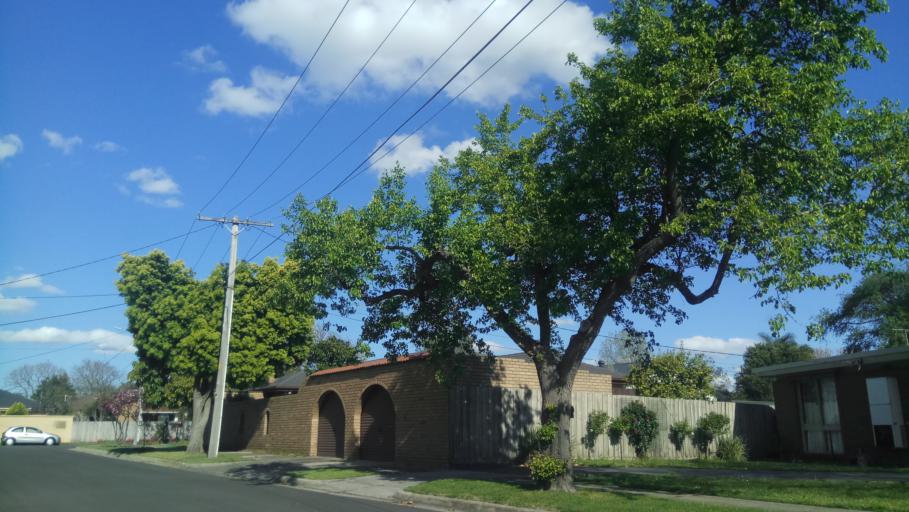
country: AU
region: Victoria
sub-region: Kingston
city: Dingley Village
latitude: -37.9838
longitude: 145.1261
